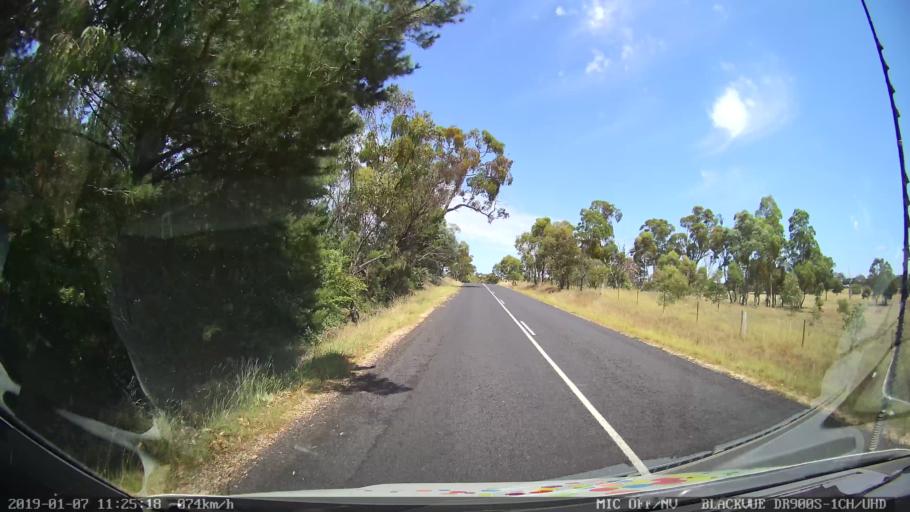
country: AU
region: New South Wales
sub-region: Armidale Dumaresq
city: Armidale
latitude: -30.4607
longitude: 151.6034
